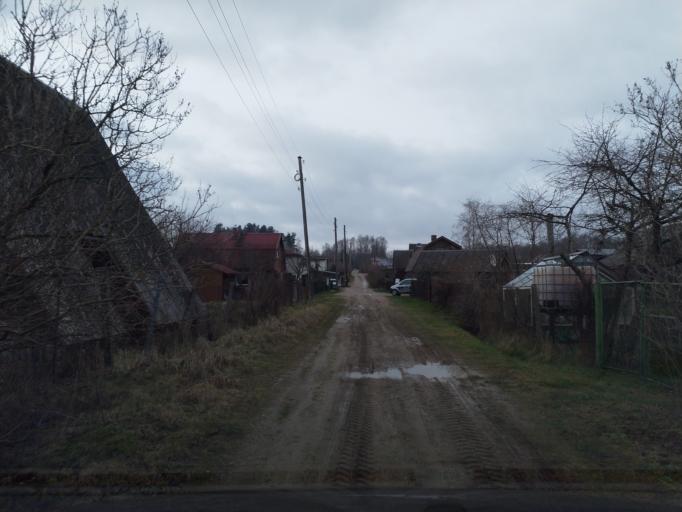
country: LV
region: Kuldigas Rajons
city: Kuldiga
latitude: 56.9469
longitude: 22.0085
